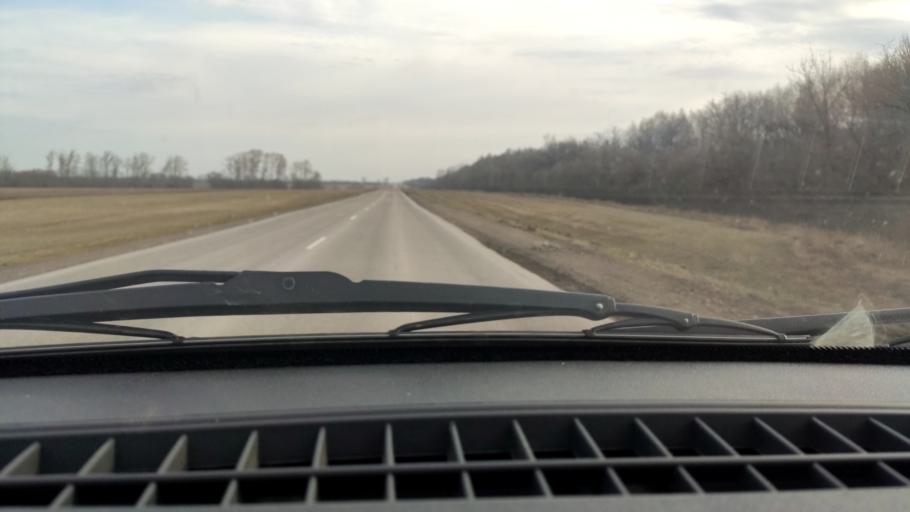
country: RU
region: Bashkortostan
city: Davlekanovo
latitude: 54.2539
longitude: 55.0837
